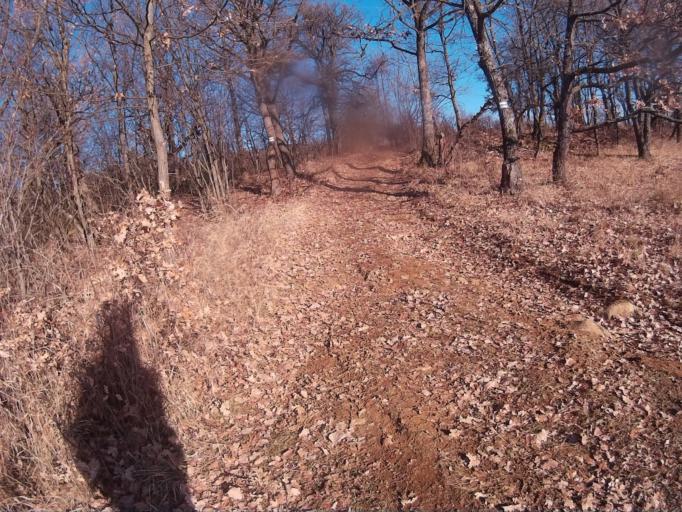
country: HU
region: Borsod-Abauj-Zemplen
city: Rudabanya
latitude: 48.4880
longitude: 20.5792
